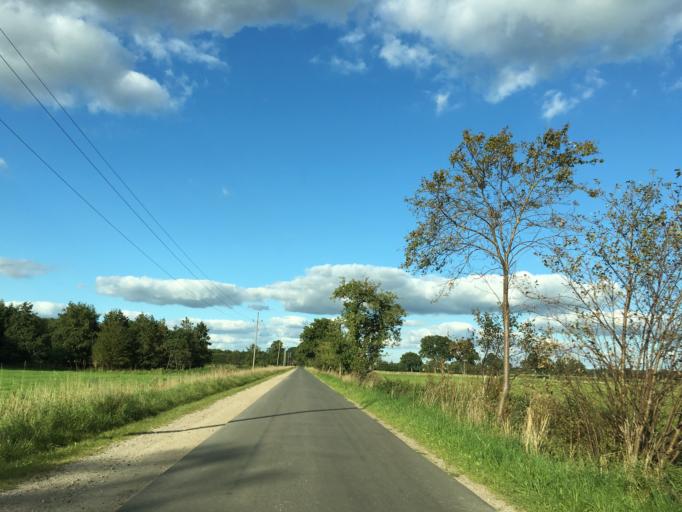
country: DE
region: Lower Saxony
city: Salzhausen
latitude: 53.2385
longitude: 10.1794
